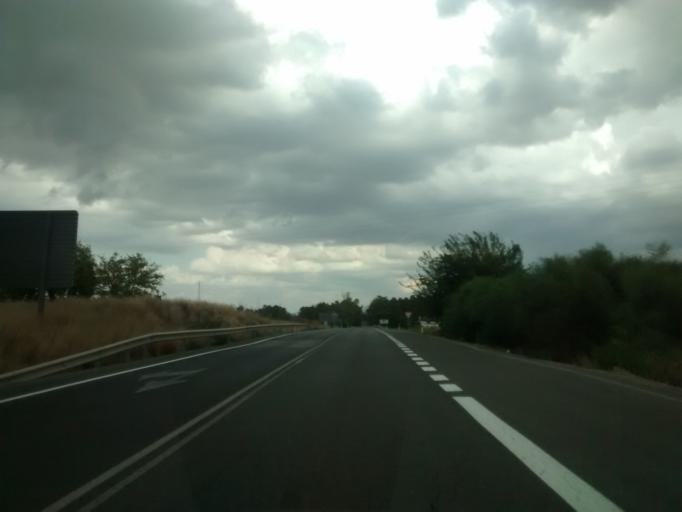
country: ES
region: Andalusia
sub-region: Provincia de Cadiz
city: Villamartin
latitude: 36.8452
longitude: -5.6877
